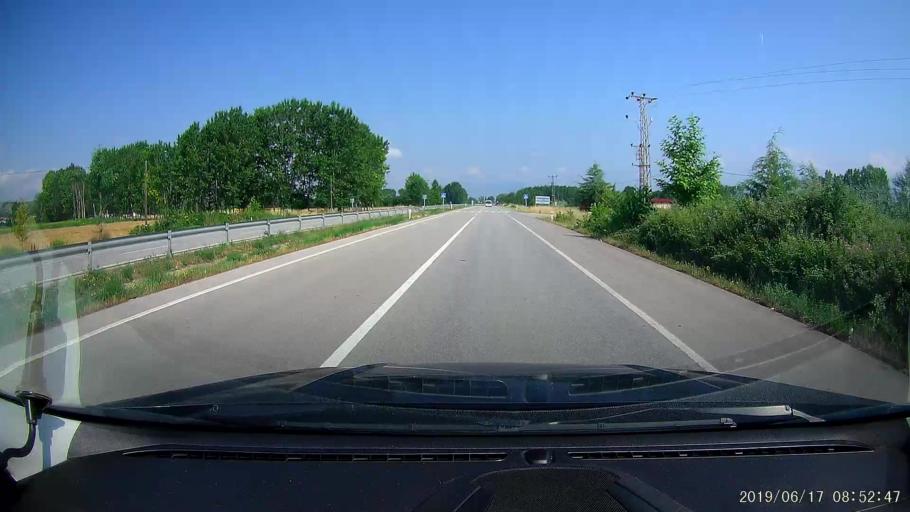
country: TR
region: Tokat
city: Erbaa
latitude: 40.7023
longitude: 36.4912
